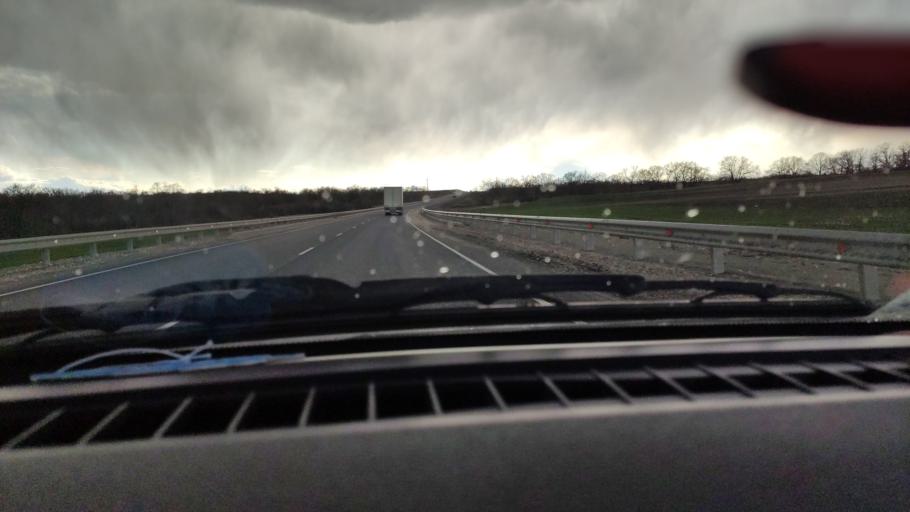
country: RU
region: Saratov
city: Yelshanka
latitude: 51.8307
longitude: 46.4489
